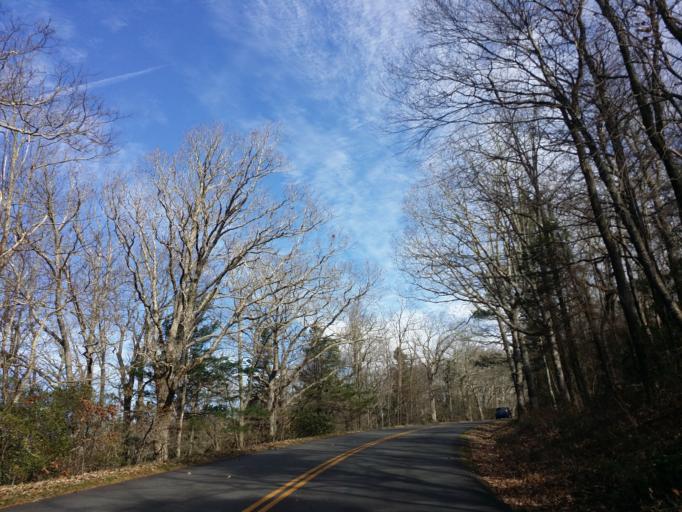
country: US
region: North Carolina
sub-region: Mitchell County
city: Spruce Pine
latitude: 35.8386
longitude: -82.1075
